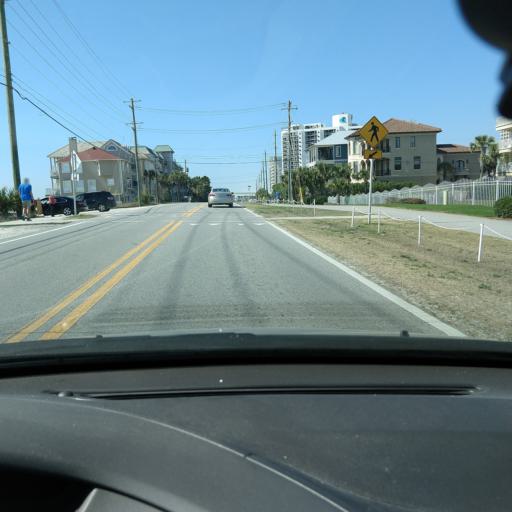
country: US
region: Florida
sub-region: Walton County
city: Miramar Beach
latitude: 30.3751
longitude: -86.3626
